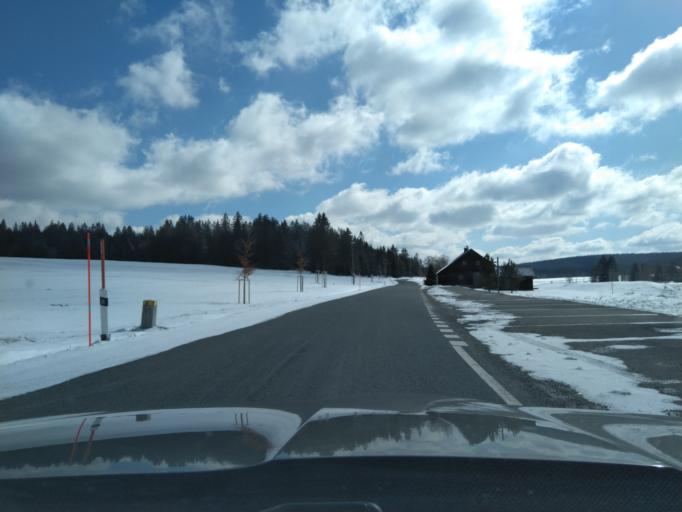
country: CZ
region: Plzensky
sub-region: Okres Klatovy
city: Kasperske Hory
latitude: 49.0514
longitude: 13.5714
